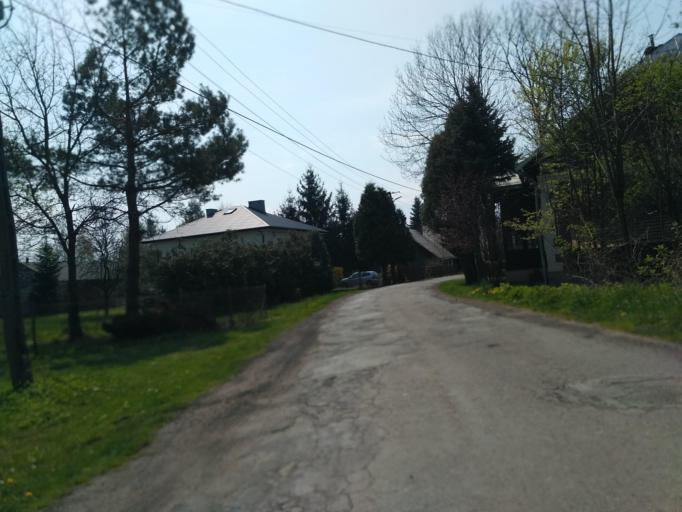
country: PL
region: Subcarpathian Voivodeship
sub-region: Powiat krosnienski
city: Chorkowka
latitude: 49.6418
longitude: 21.7219
